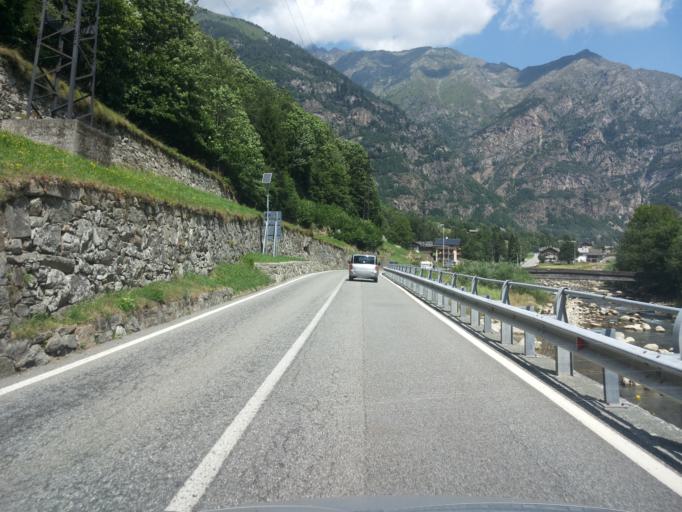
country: IT
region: Aosta Valley
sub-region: Valle d'Aosta
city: Issime
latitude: 45.6711
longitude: 7.8574
